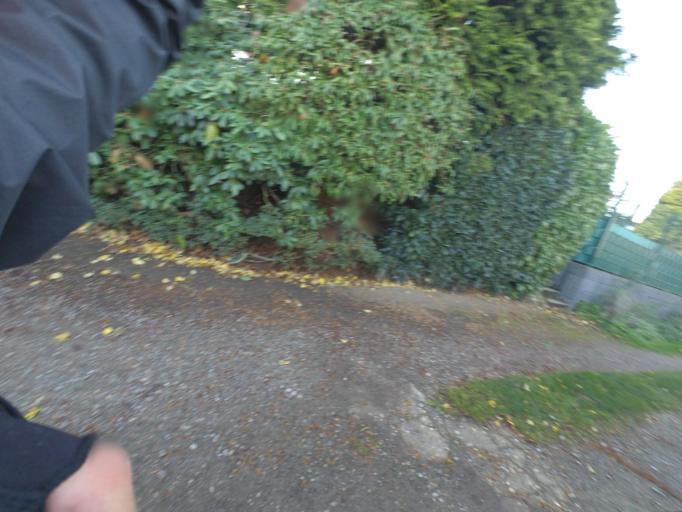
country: DE
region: North Rhine-Westphalia
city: Sprockhovel
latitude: 51.3369
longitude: 7.2888
